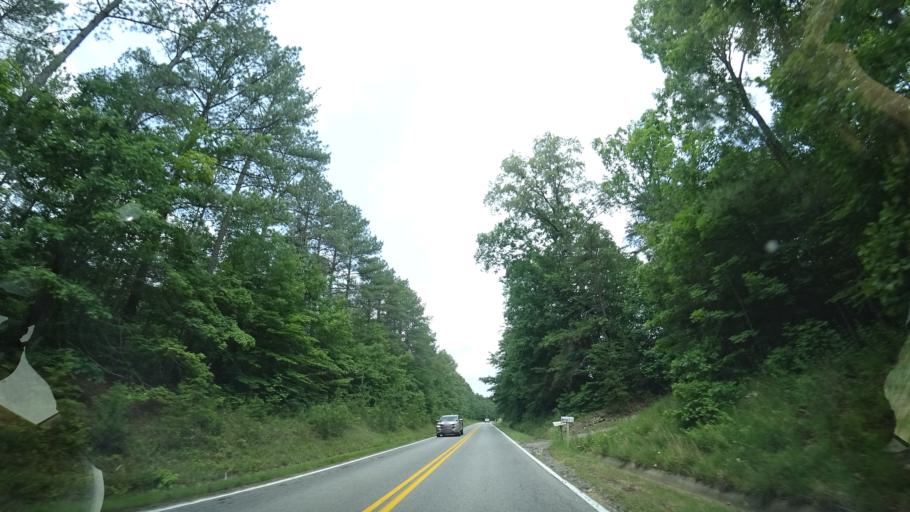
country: US
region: Virginia
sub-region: Louisa County
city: Louisa
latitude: 38.1405
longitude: -77.8093
